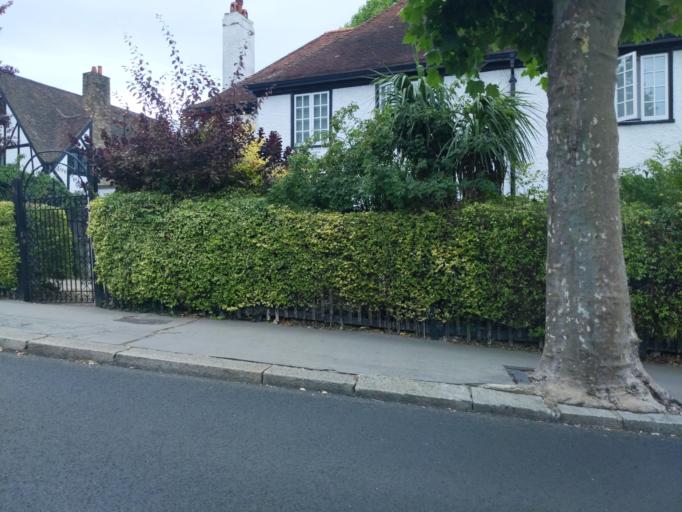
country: GB
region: England
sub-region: Greater London
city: South Croydon
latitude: 51.3559
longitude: -0.0843
